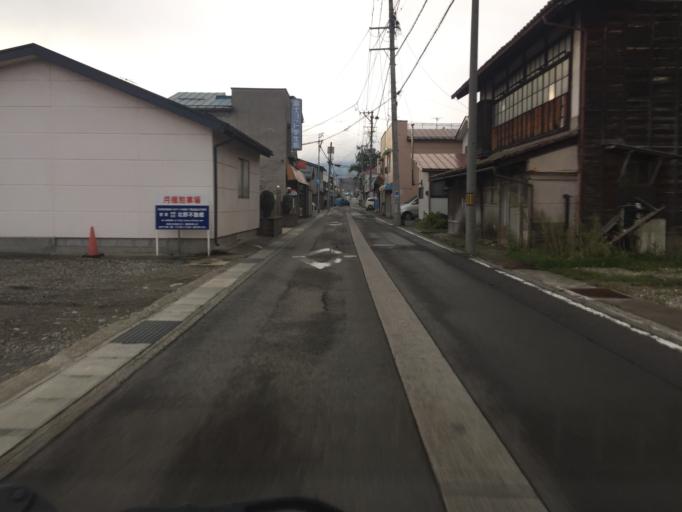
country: JP
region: Fukushima
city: Kitakata
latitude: 37.4924
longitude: 139.9111
